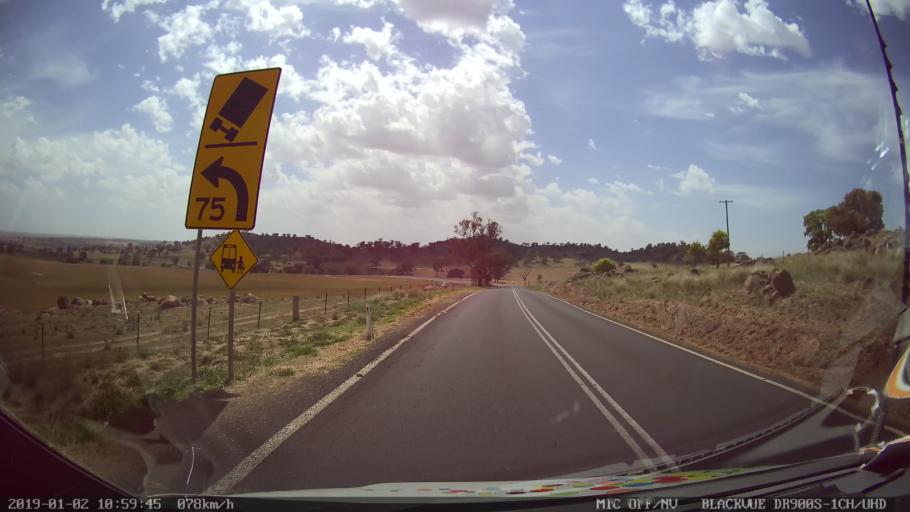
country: AU
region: New South Wales
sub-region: Cootamundra
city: Cootamundra
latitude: -34.6124
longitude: 148.3097
